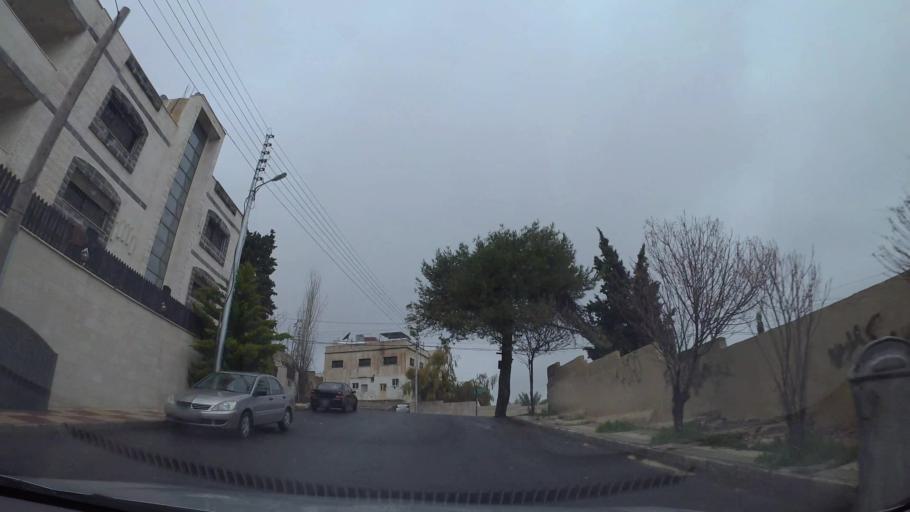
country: JO
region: Amman
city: Al Jubayhah
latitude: 32.0224
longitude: 35.8384
